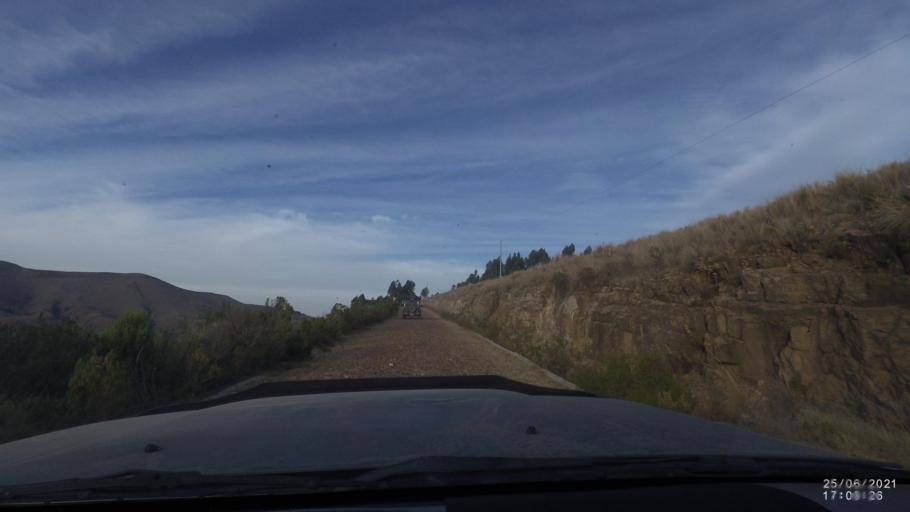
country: BO
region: Cochabamba
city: Arani
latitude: -17.8371
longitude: -65.7055
